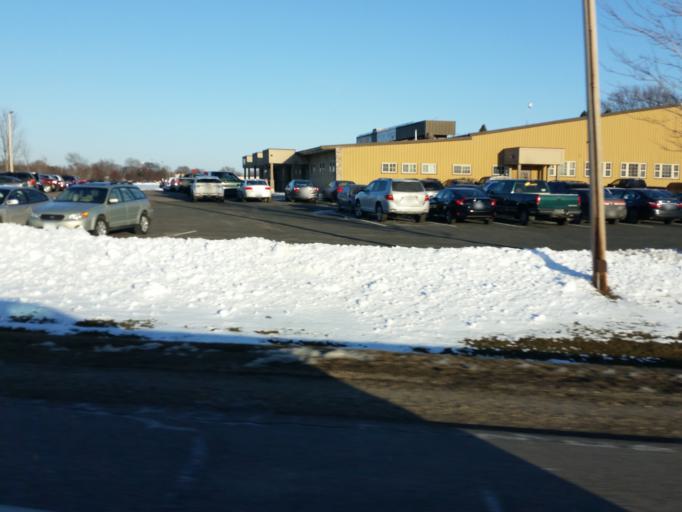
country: US
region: Minnesota
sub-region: Dakota County
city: Hastings
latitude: 44.7138
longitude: -92.8524
